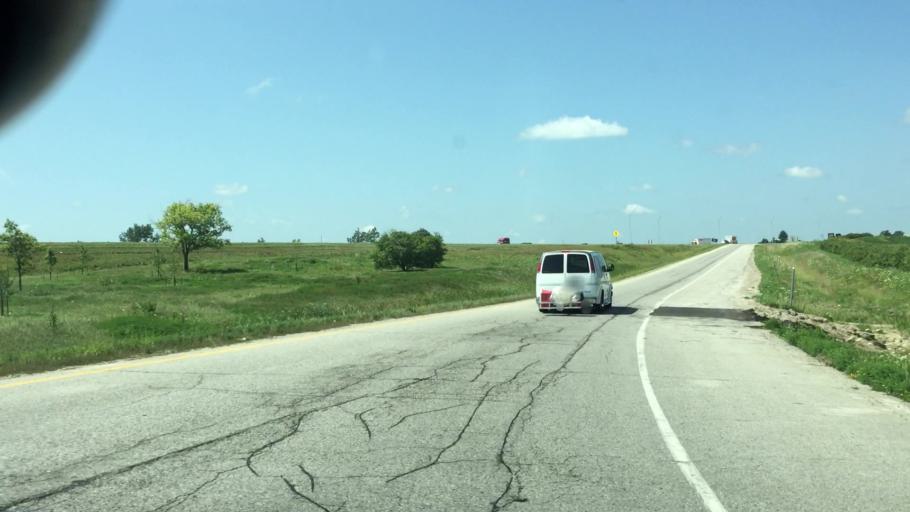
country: US
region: Iowa
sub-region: Poweshiek County
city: Grinnell
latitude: 41.6975
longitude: -92.7277
